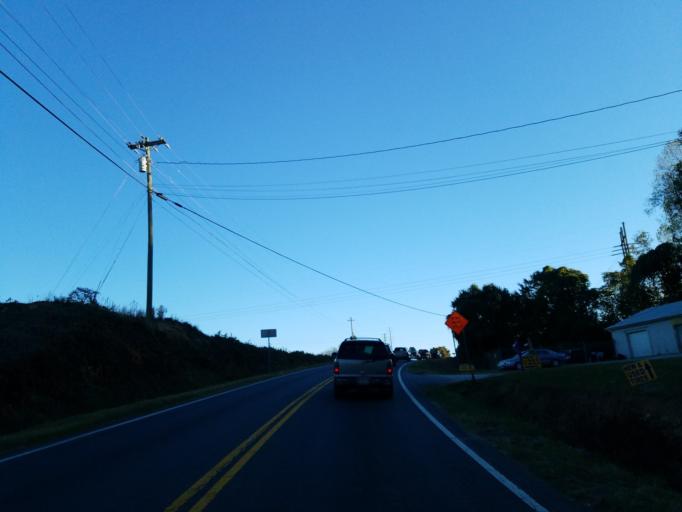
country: US
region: Georgia
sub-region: Dawson County
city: Dawsonville
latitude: 34.3717
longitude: -84.0421
